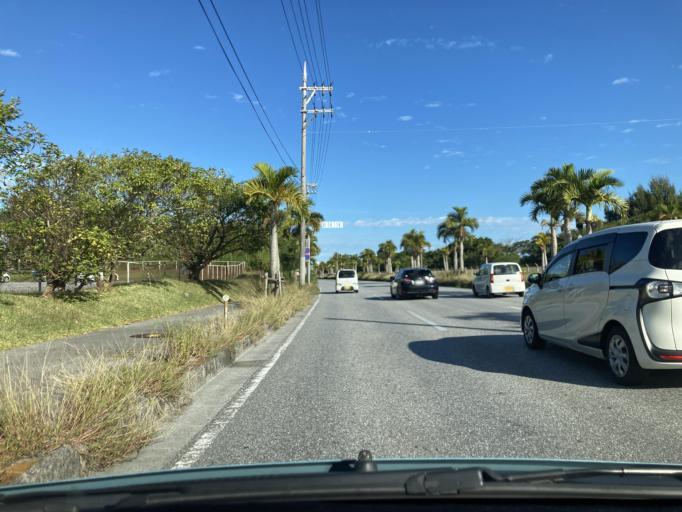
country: JP
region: Okinawa
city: Chatan
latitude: 26.3504
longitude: 127.7467
